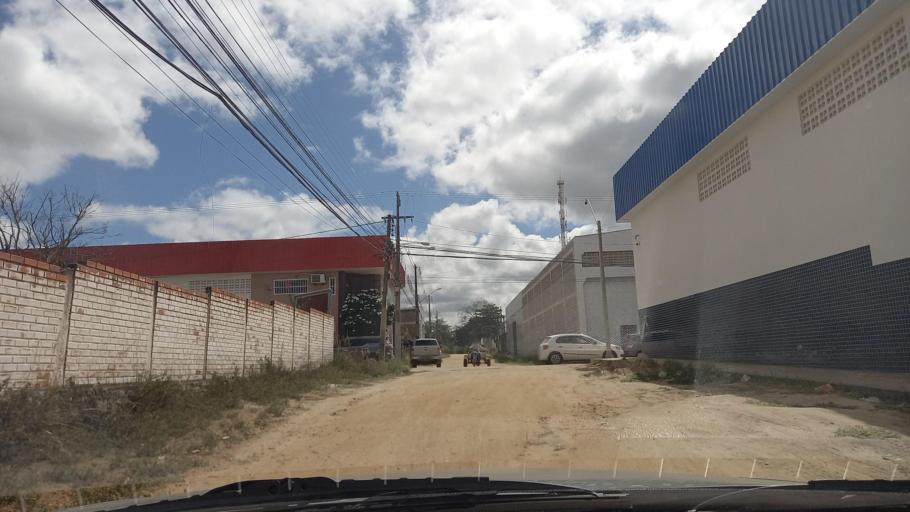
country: BR
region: Pernambuco
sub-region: Caruaru
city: Caruaru
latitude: -8.2556
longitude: -35.9773
